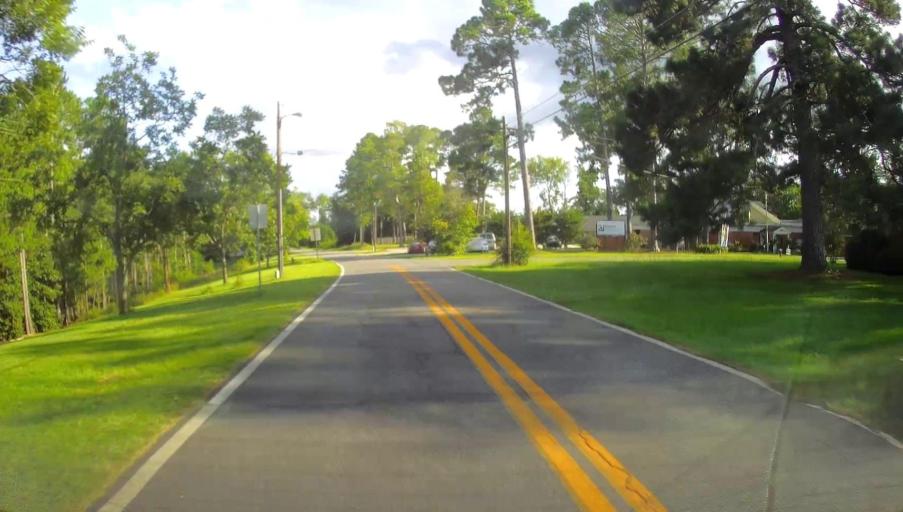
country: US
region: Georgia
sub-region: Crawford County
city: Roberta
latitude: 32.7121
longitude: -84.0182
